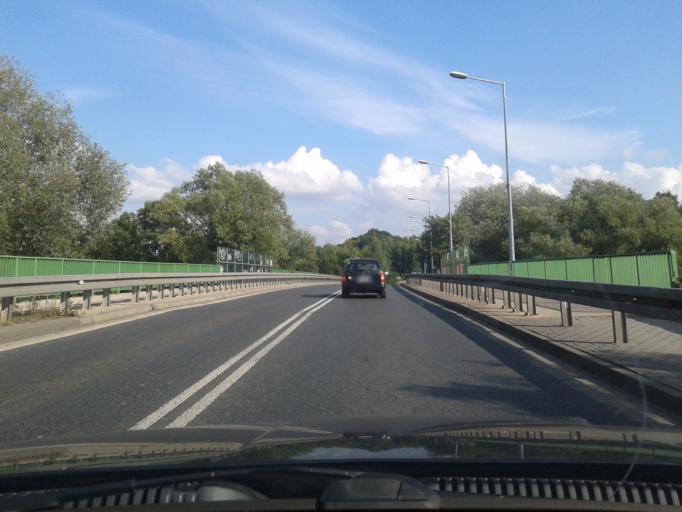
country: PL
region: Silesian Voivodeship
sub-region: Powiat wodzislawski
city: Wodzislaw Slaski
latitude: 50.0027
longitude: 18.4743
